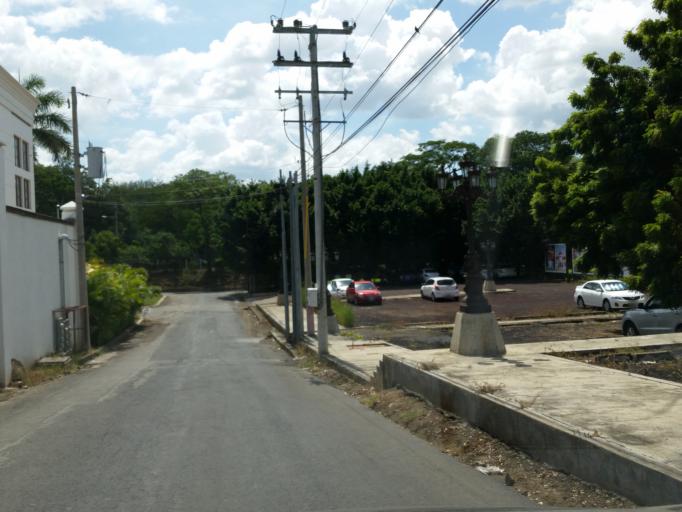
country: NI
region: Managua
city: Managua
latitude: 12.0974
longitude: -86.2474
